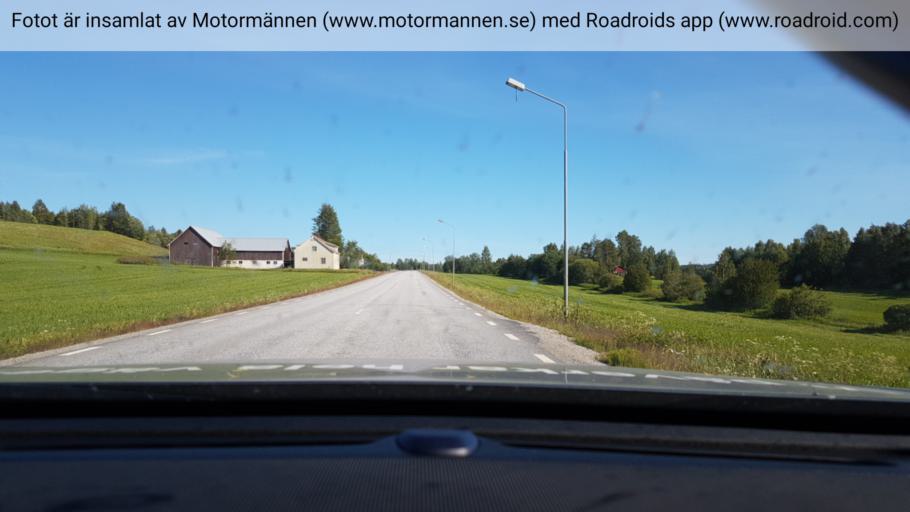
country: SE
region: Vaesterbotten
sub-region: Vindelns Kommun
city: Vindeln
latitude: 64.1718
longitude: 19.4878
